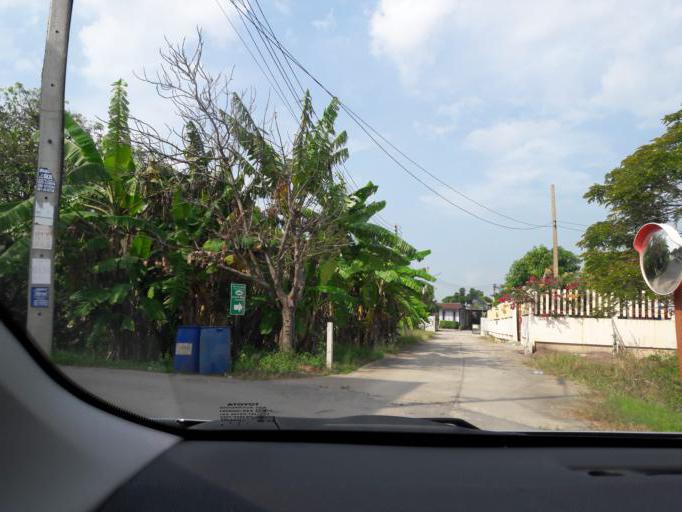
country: TH
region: Ang Thong
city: Ang Thong
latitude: 14.5977
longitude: 100.4350
